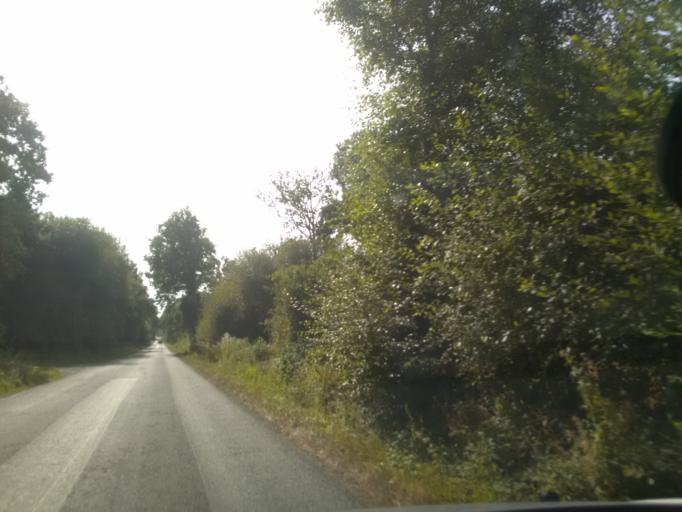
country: FR
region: Brittany
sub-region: Departement d'Ille-et-Vilaine
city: Quebriac
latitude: 48.3519
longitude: -1.7714
